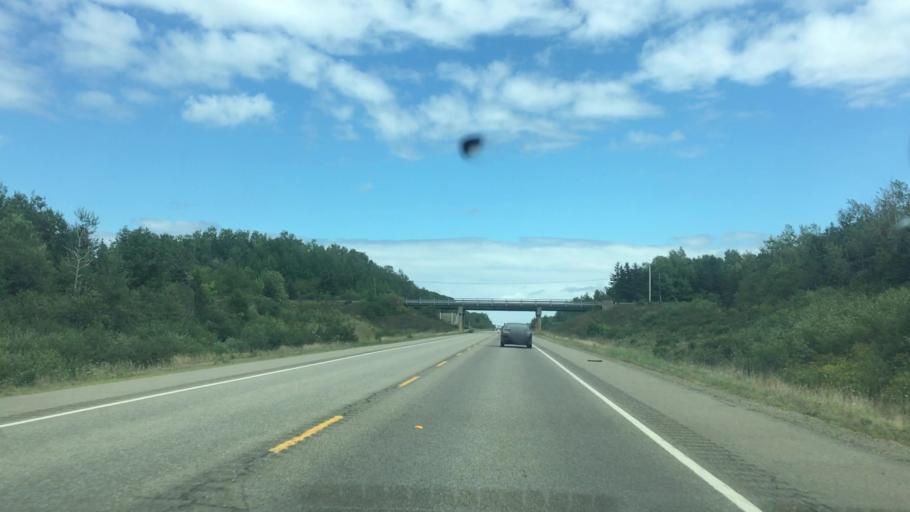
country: CA
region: Nova Scotia
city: Port Hawkesbury
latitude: 45.6187
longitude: -61.6152
